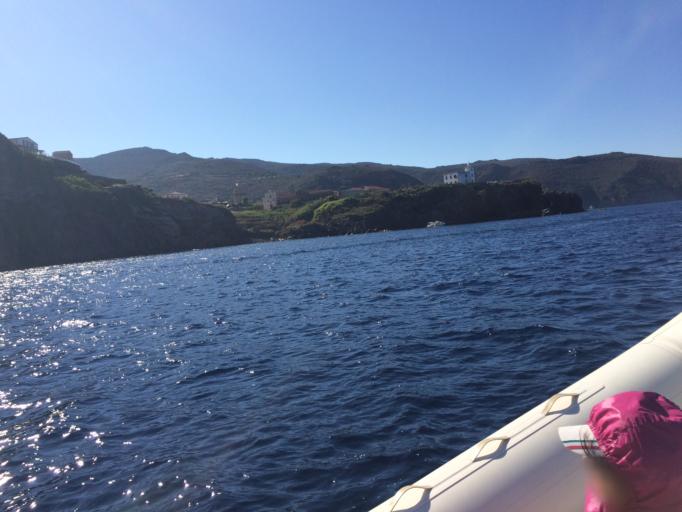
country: IT
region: Tuscany
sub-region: Provincia di Livorno
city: Capraia Isola
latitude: 43.0490
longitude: 9.8476
